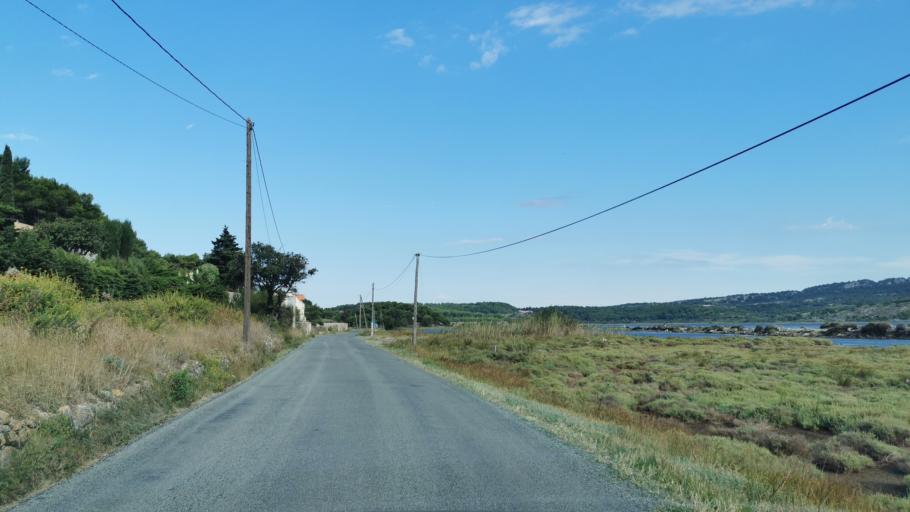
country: FR
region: Languedoc-Roussillon
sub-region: Departement de l'Aude
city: Gruissan
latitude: 43.1052
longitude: 3.0810
